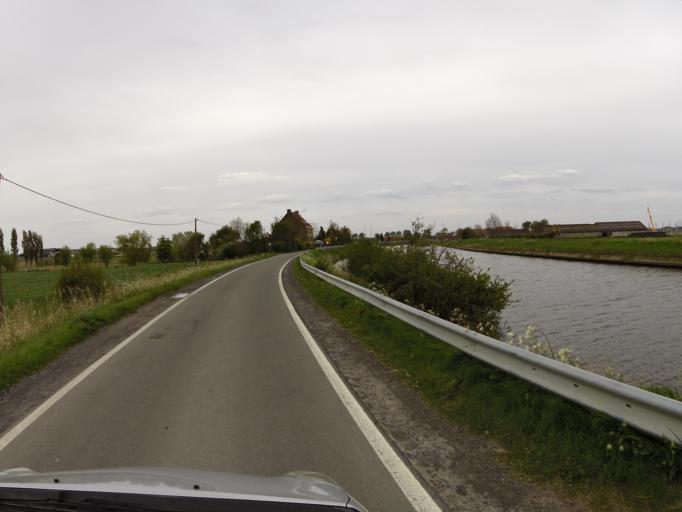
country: BE
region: Flanders
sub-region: Provincie West-Vlaanderen
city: Diksmuide
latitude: 51.0793
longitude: 2.8376
